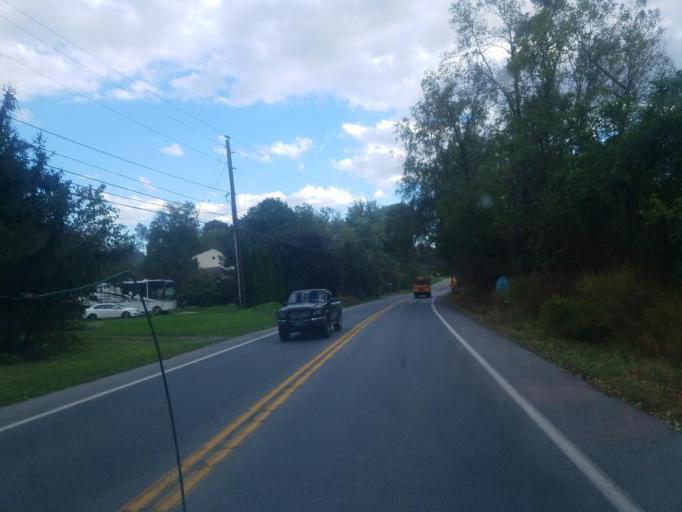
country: US
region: Pennsylvania
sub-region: Dauphin County
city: Middletown
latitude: 40.1658
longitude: -76.7191
